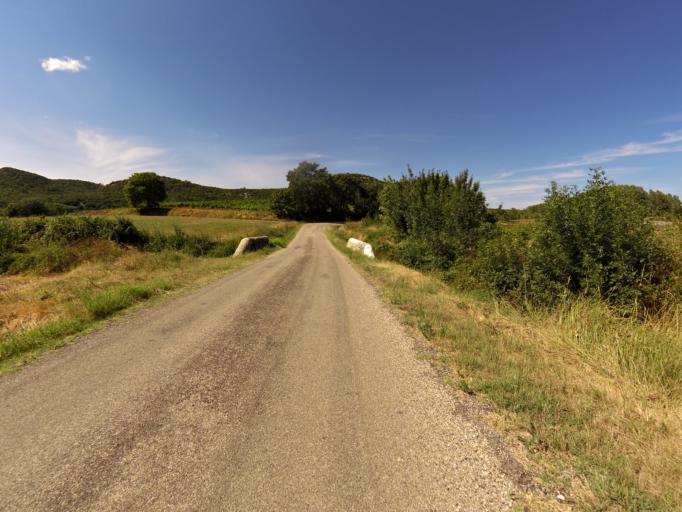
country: FR
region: Languedoc-Roussillon
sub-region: Departement du Gard
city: Quissac
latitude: 43.9214
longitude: 4.0454
